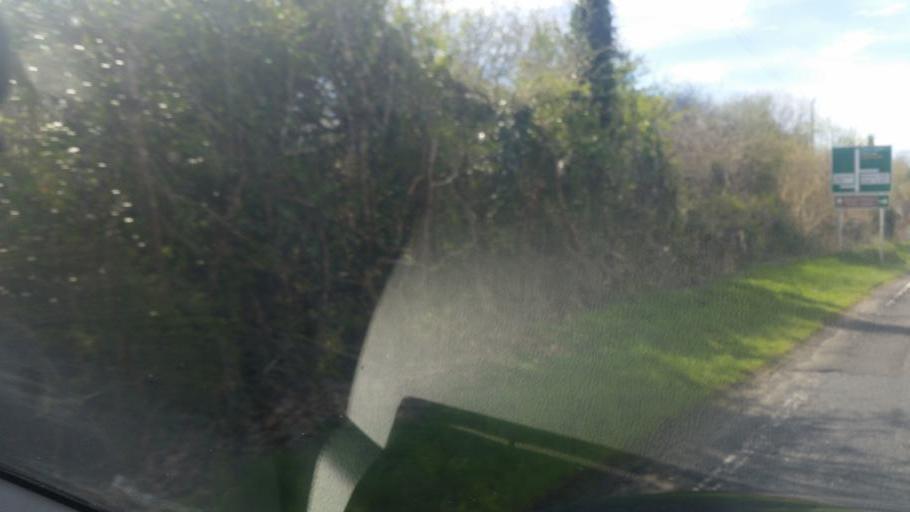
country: IE
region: Ulster
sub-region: County Donegal
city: Ballyshannon
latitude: 54.4747
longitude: -8.0903
